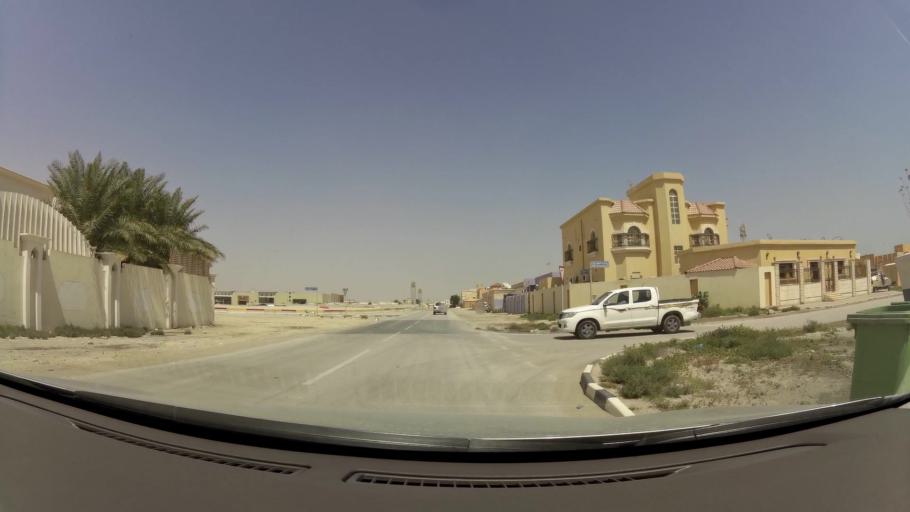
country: QA
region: Baladiyat Umm Salal
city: Umm Salal Muhammad
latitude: 25.3667
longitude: 51.4757
